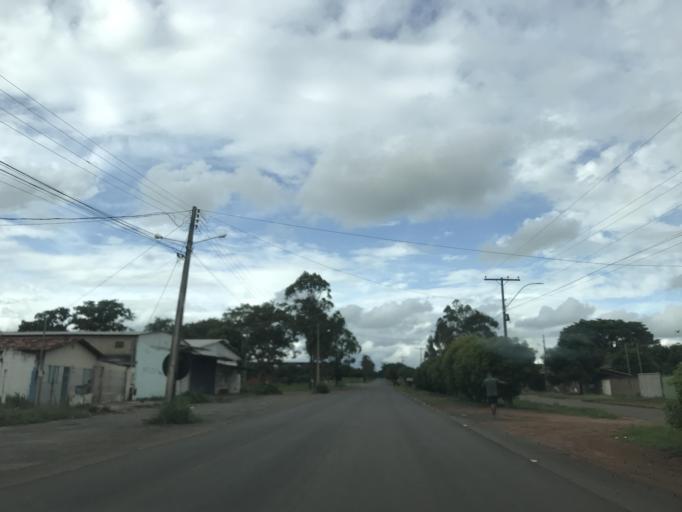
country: BR
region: Goias
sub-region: Bela Vista De Goias
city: Bela Vista de Goias
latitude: -17.0493
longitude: -48.6648
